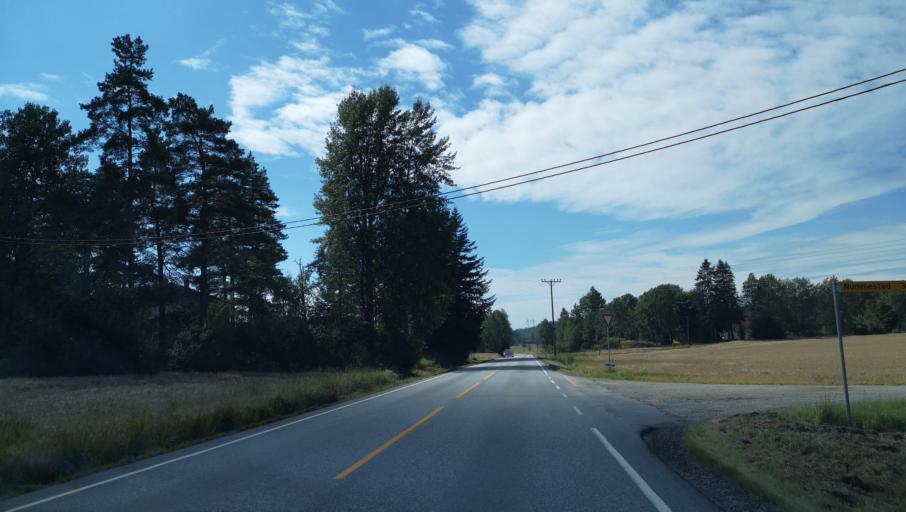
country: NO
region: Akershus
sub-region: Vestby
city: Vestby
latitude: 59.5461
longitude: 10.7941
